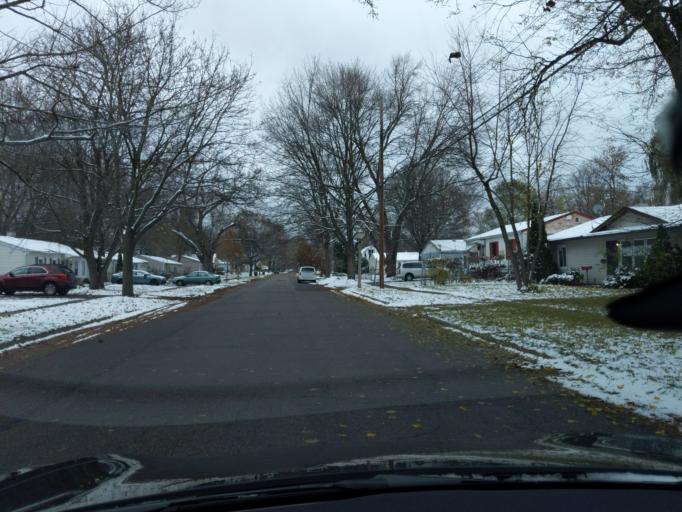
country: US
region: Michigan
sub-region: Ingham County
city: Lansing
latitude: 42.6916
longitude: -84.5916
